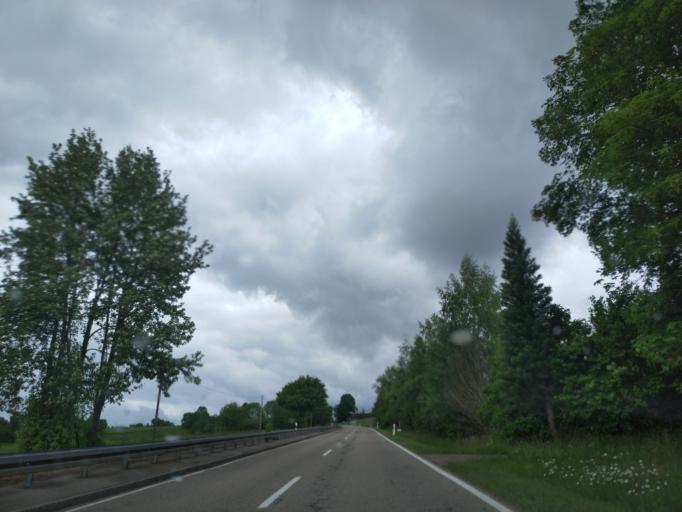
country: DE
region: Baden-Wuerttemberg
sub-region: Freiburg Region
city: Loffingen
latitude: 47.8532
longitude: 8.3169
